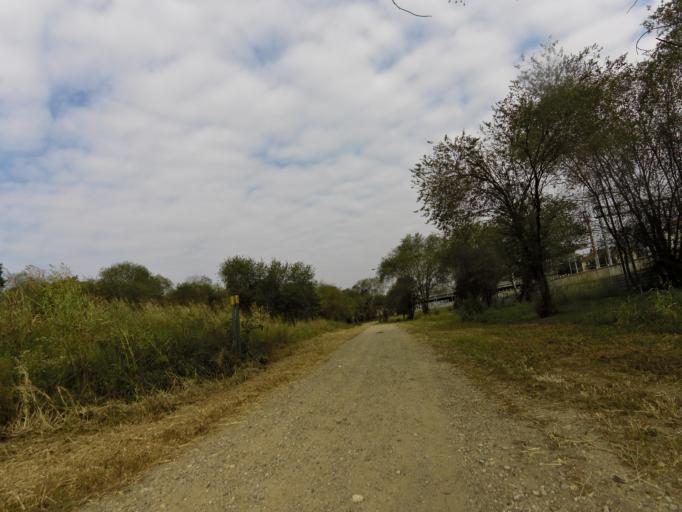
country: IT
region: Lombardy
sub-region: Citta metropolitana di Milano
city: Chiaravalle
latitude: 45.4293
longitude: 9.2400
